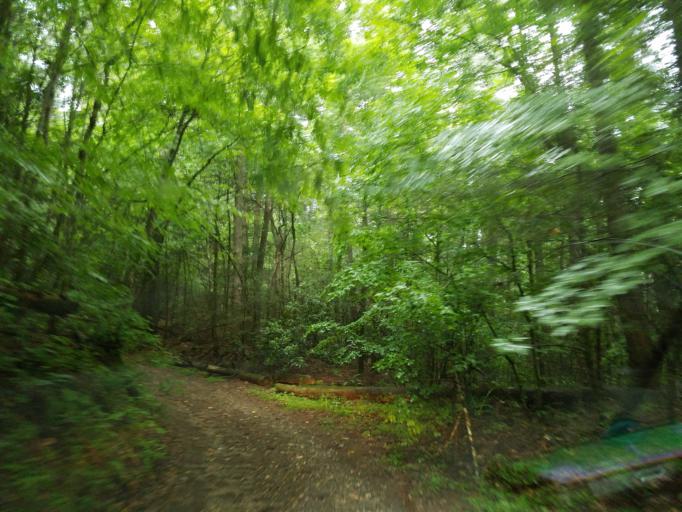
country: US
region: Georgia
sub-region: Lumpkin County
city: Dahlonega
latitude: 34.6902
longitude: -84.0669
